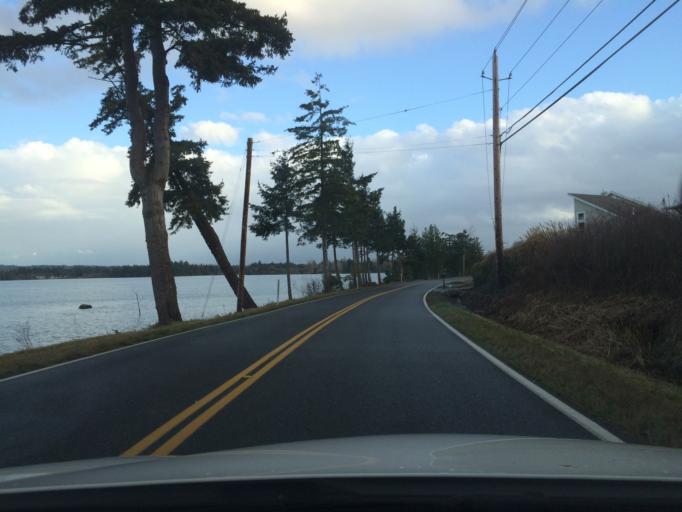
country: US
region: Washington
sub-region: Whatcom County
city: Blaine
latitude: 48.9609
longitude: -122.7580
